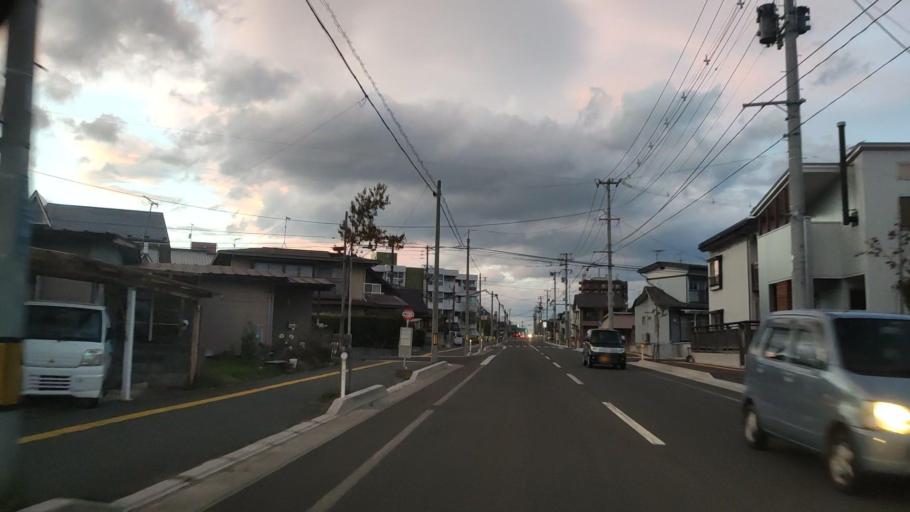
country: JP
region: Iwate
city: Morioka-shi
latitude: 39.7193
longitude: 141.1084
